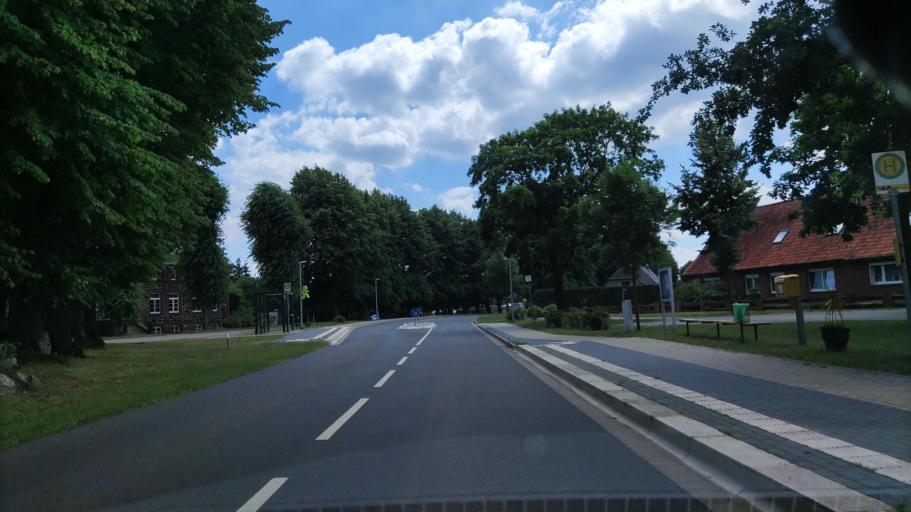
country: DE
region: Mecklenburg-Vorpommern
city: Hagenow
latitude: 53.3789
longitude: 11.1497
